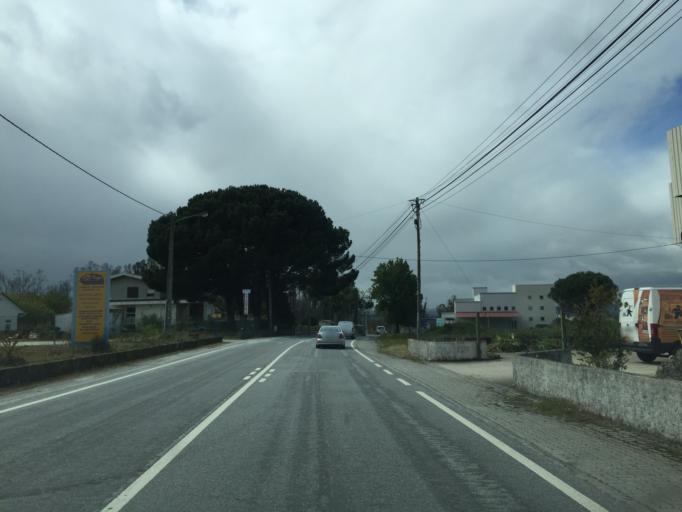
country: PT
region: Guarda
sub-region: Seia
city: Seia
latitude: 40.5081
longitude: -7.6230
